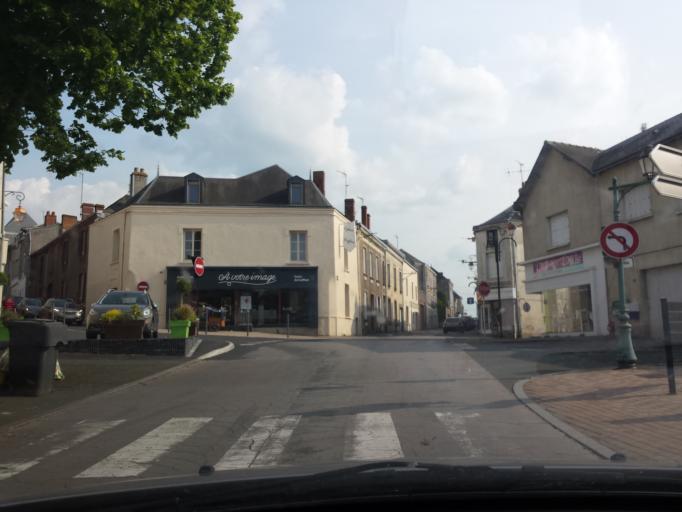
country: FR
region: Pays de la Loire
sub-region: Departement de Maine-et-Loire
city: Chemille-Melay
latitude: 47.2105
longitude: -0.7292
